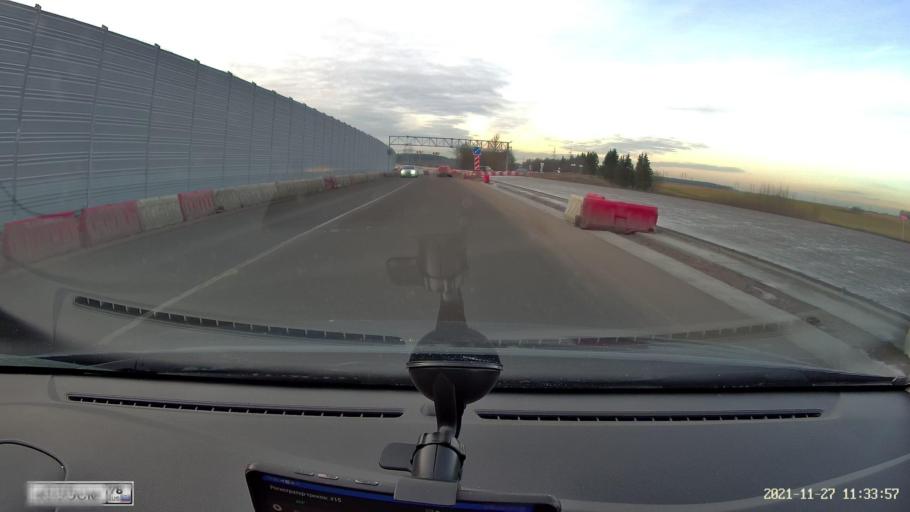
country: RU
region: Leningrad
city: Russko-Vysotskoye
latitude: 59.7082
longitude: 30.0089
